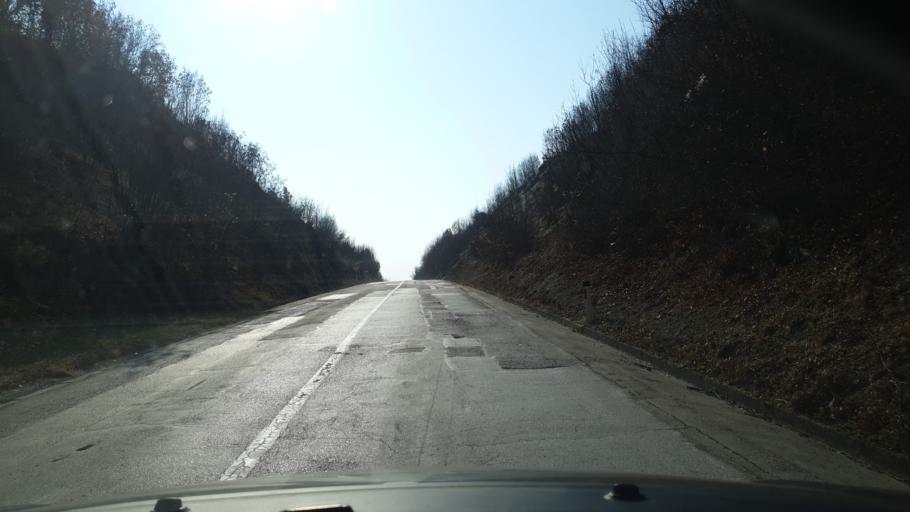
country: RS
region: Central Serbia
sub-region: Zajecarski Okrug
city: Zajecar
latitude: 43.7695
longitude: 22.3110
